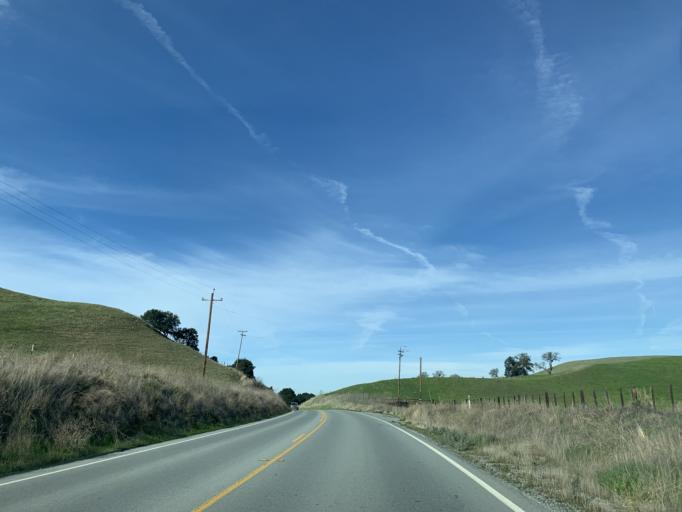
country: US
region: California
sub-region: San Benito County
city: Ridgemark
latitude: 36.7517
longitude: -121.2883
